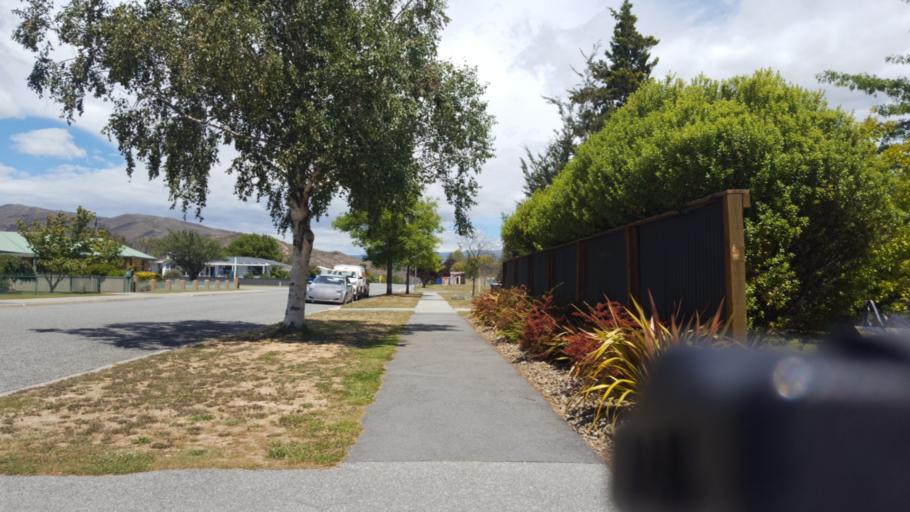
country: NZ
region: Otago
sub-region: Queenstown-Lakes District
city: Wanaka
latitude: -45.0428
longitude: 169.2053
